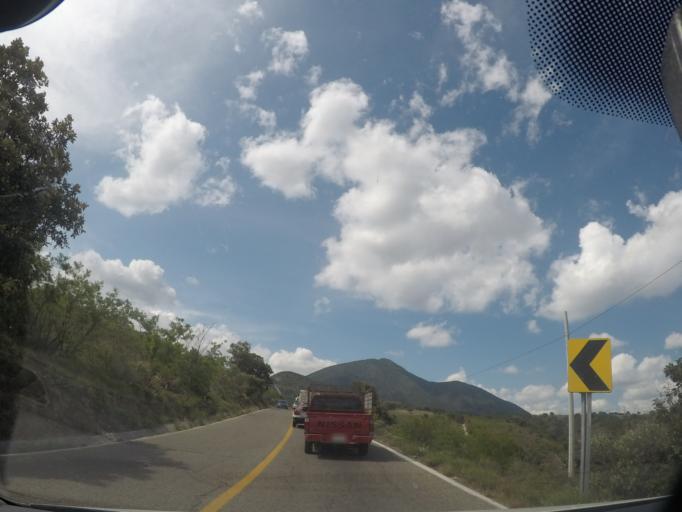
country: MX
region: Oaxaca
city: San Dionisio Ocotepec
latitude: 16.8047
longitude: -96.3507
